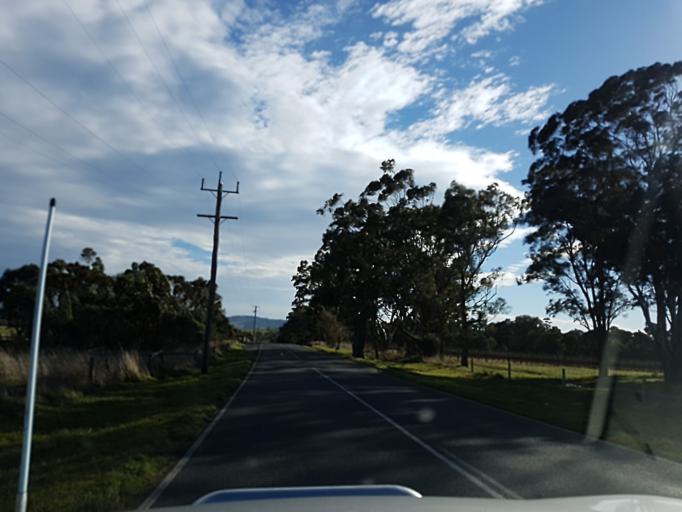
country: AU
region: Victoria
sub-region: Yarra Ranges
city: Yarra Glen
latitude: -37.6545
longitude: 145.4343
